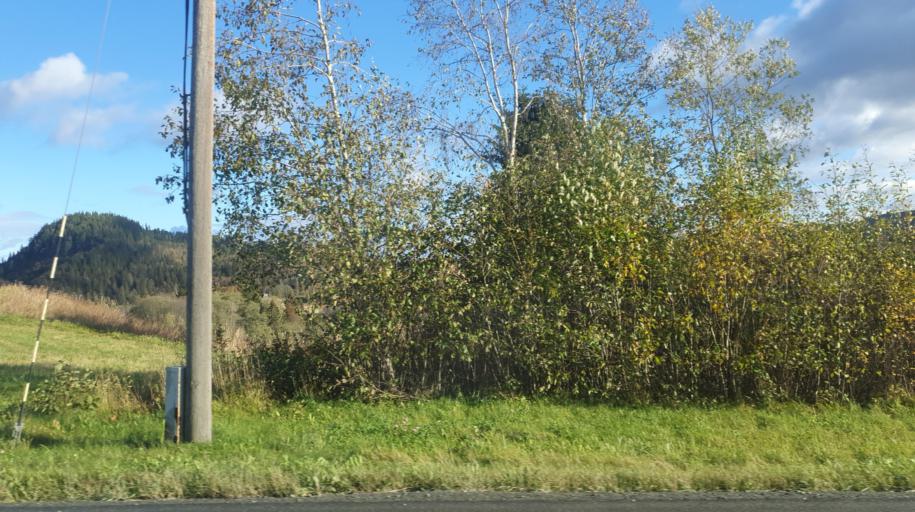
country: NO
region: Sor-Trondelag
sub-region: Klaebu
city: Klaebu
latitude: 63.3128
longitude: 10.4404
